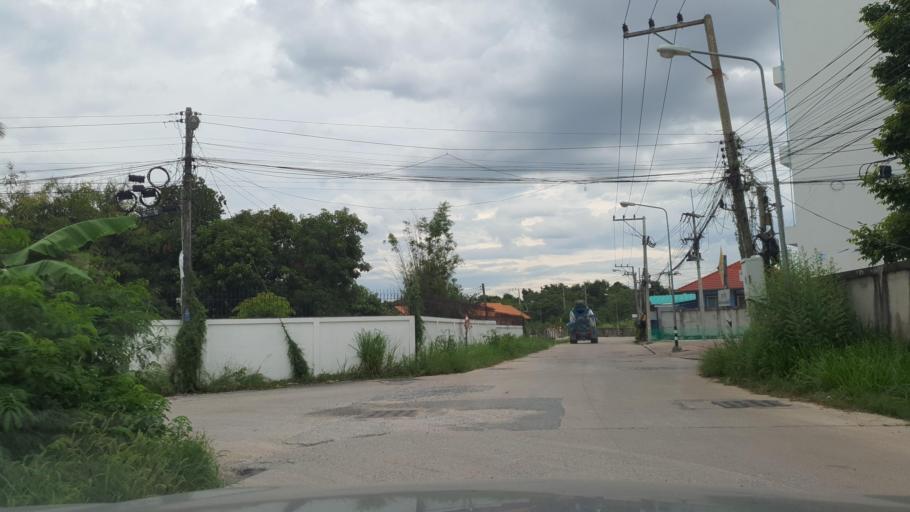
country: TH
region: Chon Buri
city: Phatthaya
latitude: 12.8785
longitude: 100.9039
